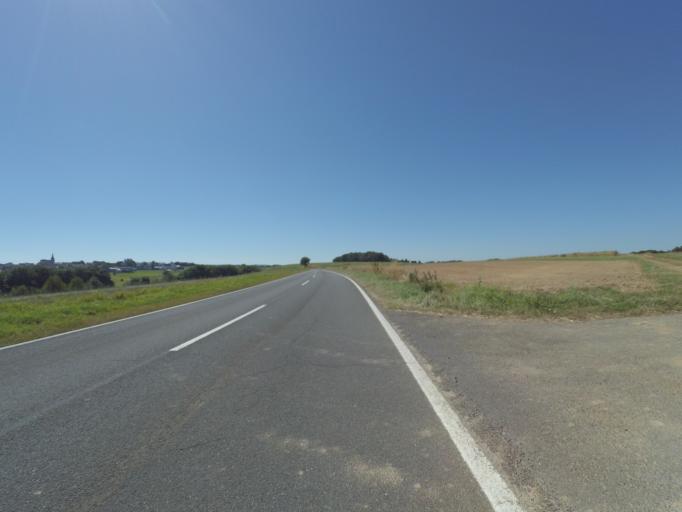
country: DE
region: Rheinland-Pfalz
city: Kliding
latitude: 50.1139
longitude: 7.0535
